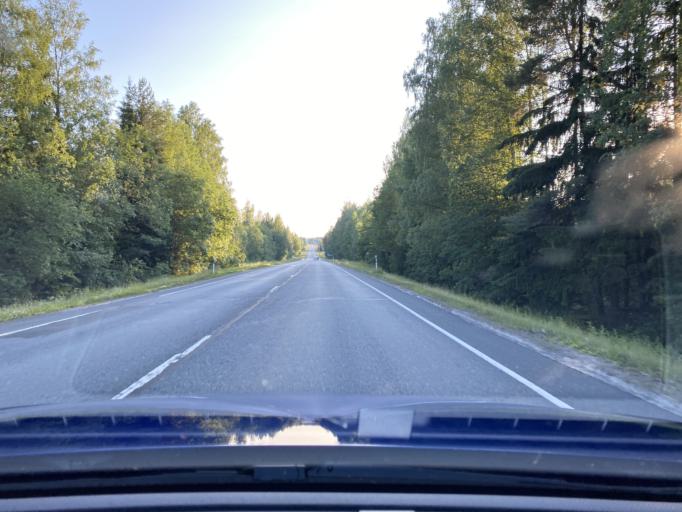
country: FI
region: Haeme
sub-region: Forssa
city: Tammela
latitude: 60.8298
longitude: 23.8525
